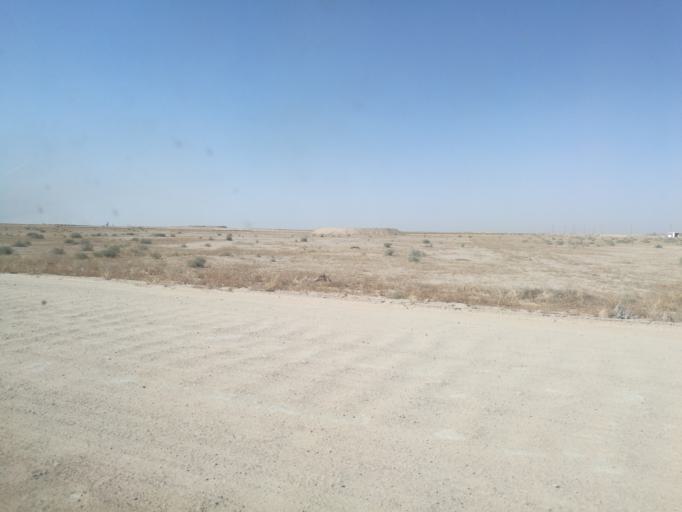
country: IQ
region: Basra Governorate
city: Az Zubayr
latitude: 30.1586
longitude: 47.4284
